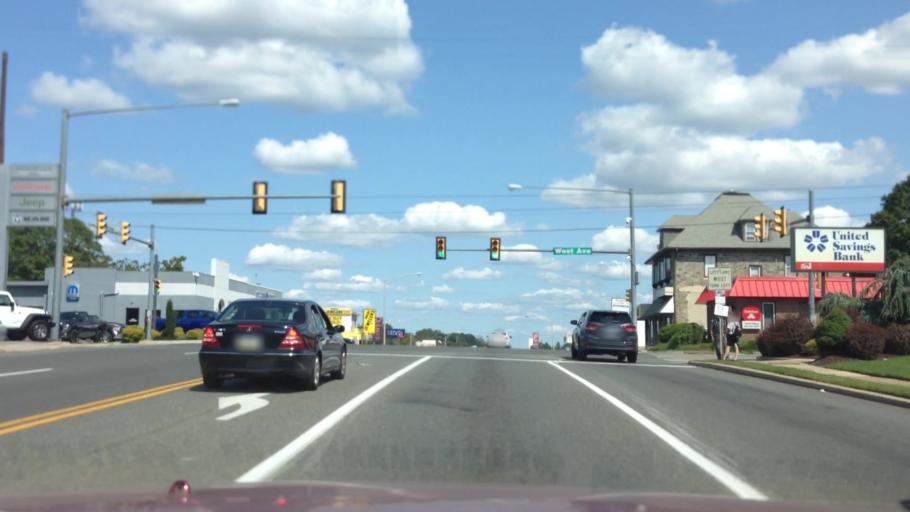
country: US
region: Pennsylvania
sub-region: Delaware County
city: Springfield
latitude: 39.9222
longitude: -75.3190
